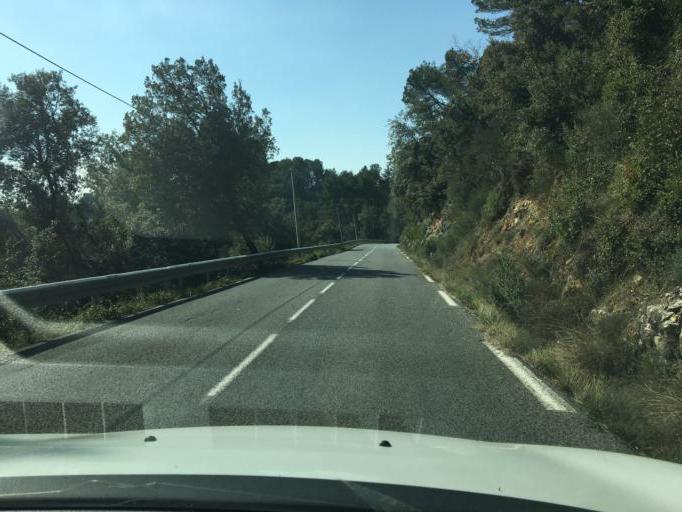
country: FR
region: Provence-Alpes-Cote d'Azur
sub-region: Departement du Var
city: Callas
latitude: 43.5998
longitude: 6.5493
